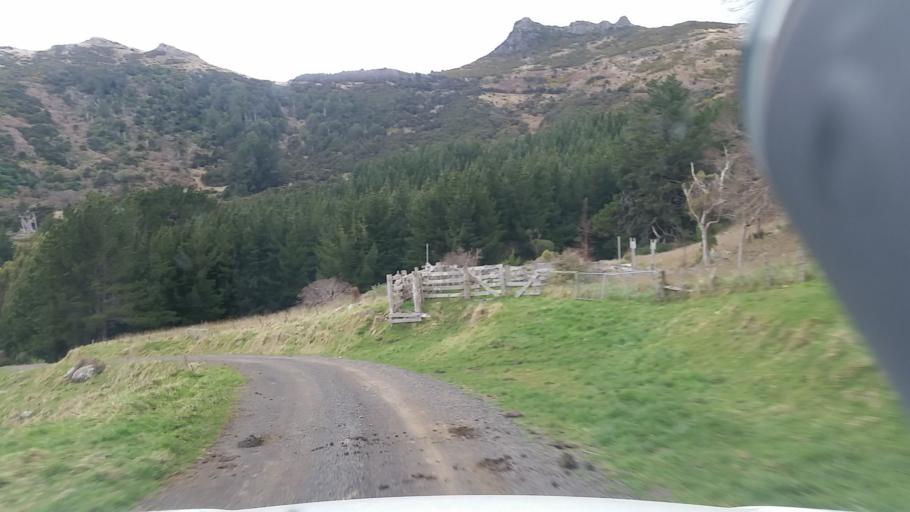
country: NZ
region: Canterbury
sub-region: Christchurch City
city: Christchurch
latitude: -43.8236
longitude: 172.9855
